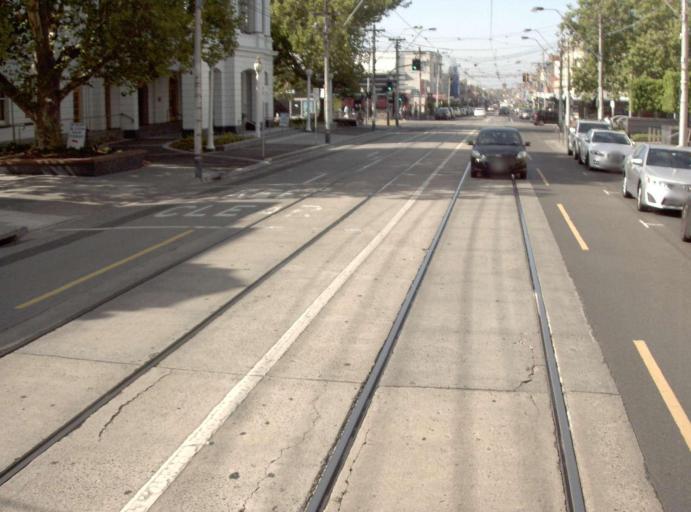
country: AU
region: Victoria
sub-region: Glen Eira
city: Caulfield North
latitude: -37.8558
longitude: 145.0294
